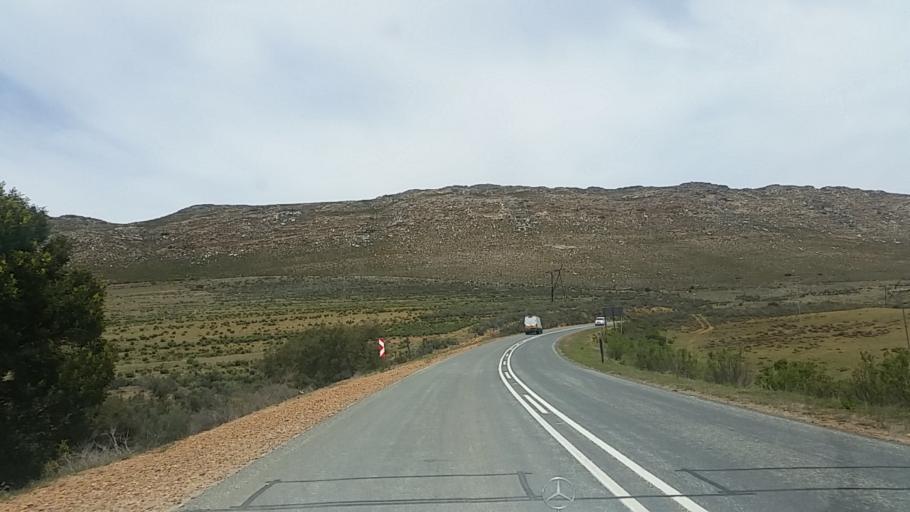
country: ZA
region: Western Cape
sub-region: Eden District Municipality
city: Knysna
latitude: -33.7375
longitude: 23.0395
